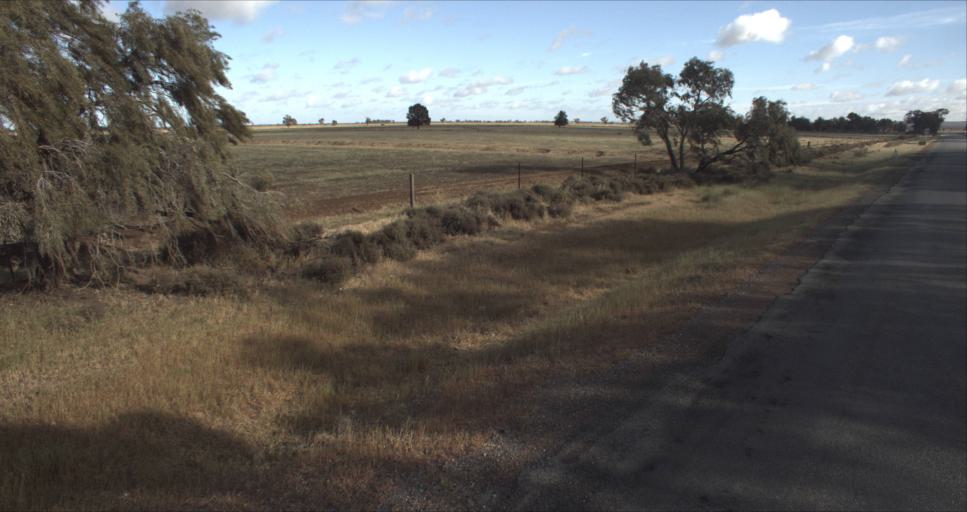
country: AU
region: New South Wales
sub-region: Leeton
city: Leeton
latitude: -34.5071
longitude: 146.3929
